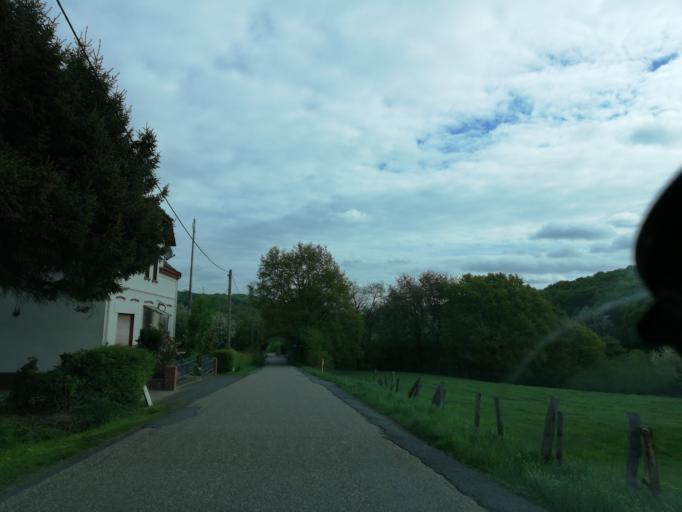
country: DE
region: North Rhine-Westphalia
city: Gevelsberg
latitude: 51.3664
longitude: 7.3088
